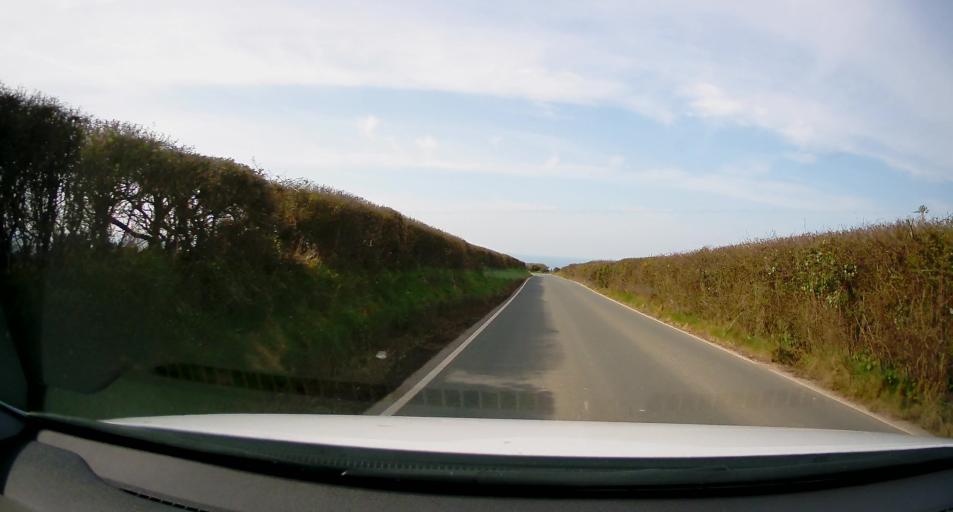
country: GB
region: Wales
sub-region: County of Ceredigion
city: Llanon
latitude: 52.2547
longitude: -4.2139
